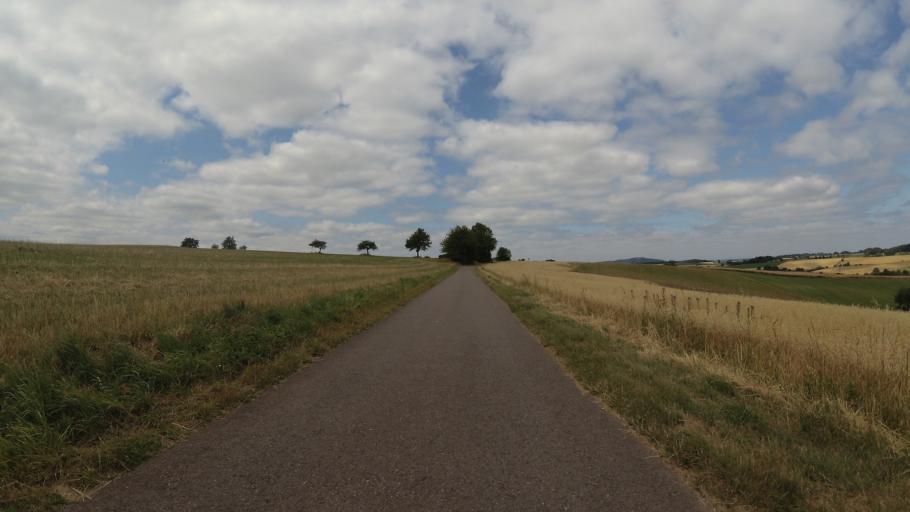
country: DE
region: Saarland
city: Mainzweiler
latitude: 49.4223
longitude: 7.0932
